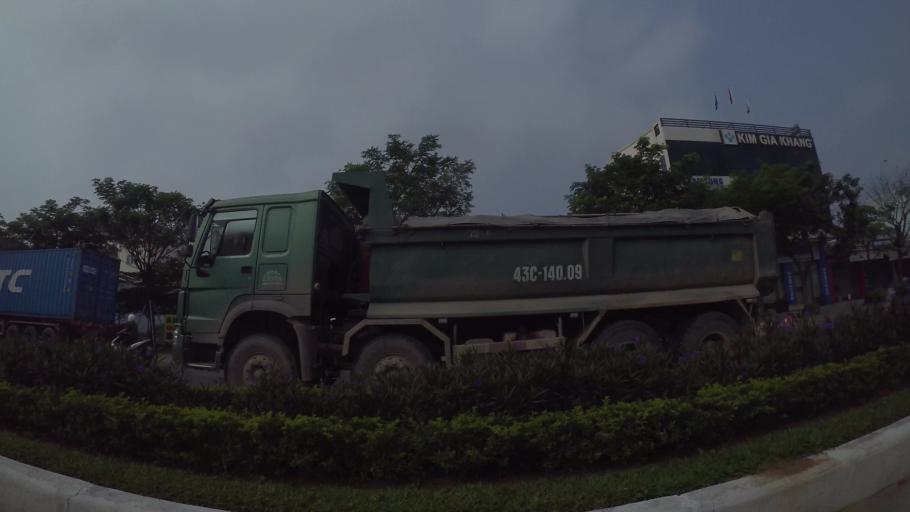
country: VN
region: Da Nang
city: Cam Le
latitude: 16.0098
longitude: 108.2179
